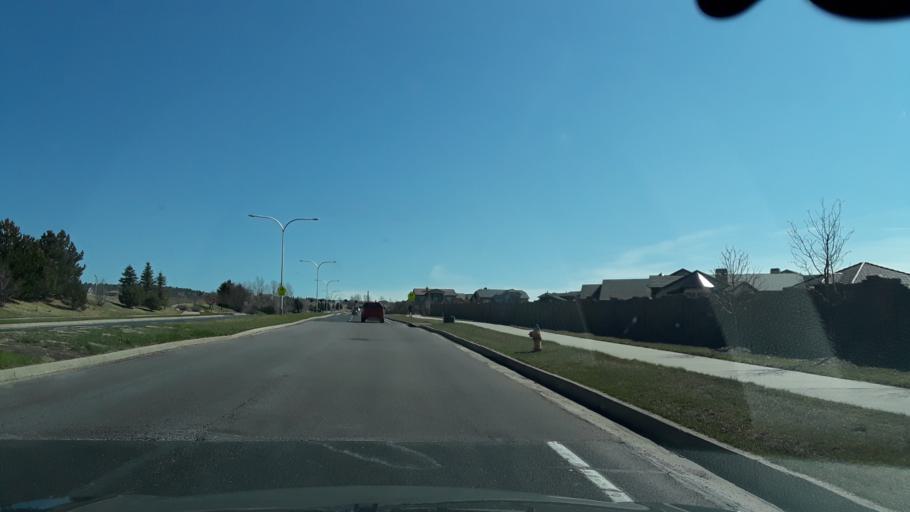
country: US
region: Colorado
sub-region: El Paso County
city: Gleneagle
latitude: 39.0276
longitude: -104.7971
